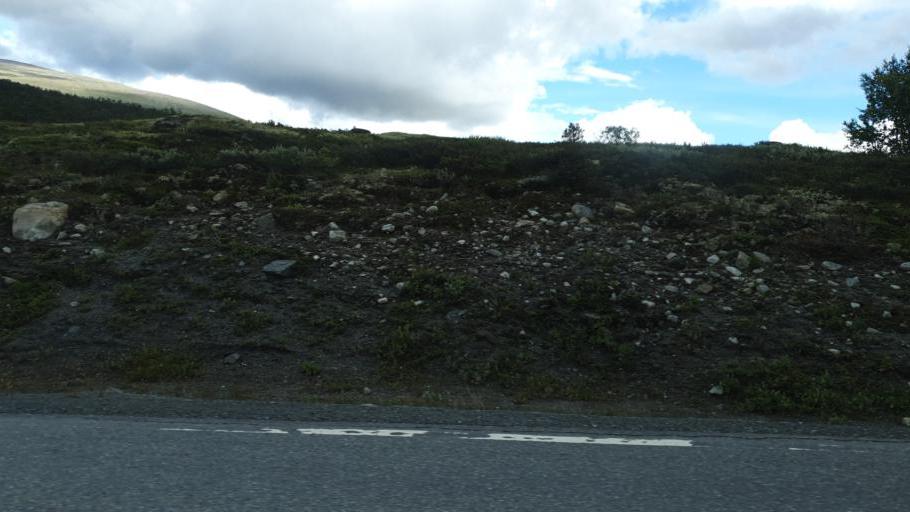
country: NO
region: Sor-Trondelag
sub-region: Oppdal
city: Oppdal
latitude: 62.2837
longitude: 9.5996
